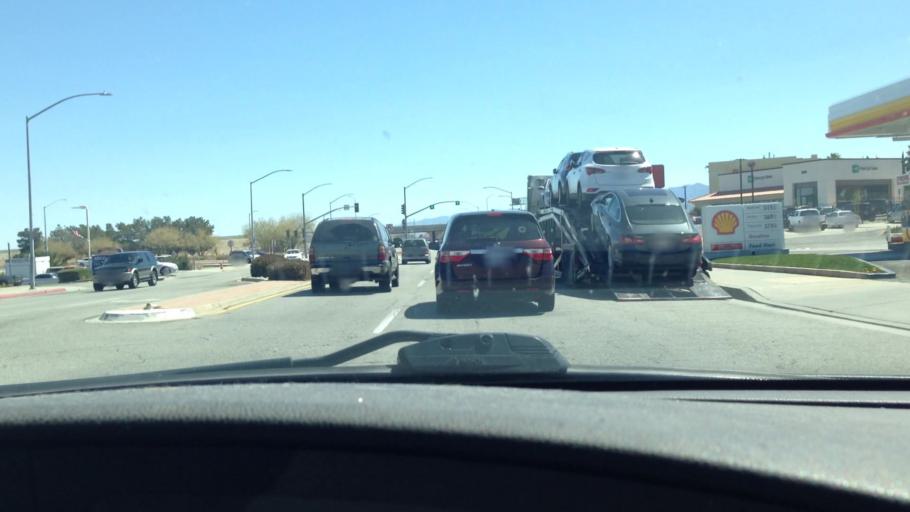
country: US
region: California
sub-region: Los Angeles County
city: Desert View Highlands
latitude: 34.5826
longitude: -118.1369
